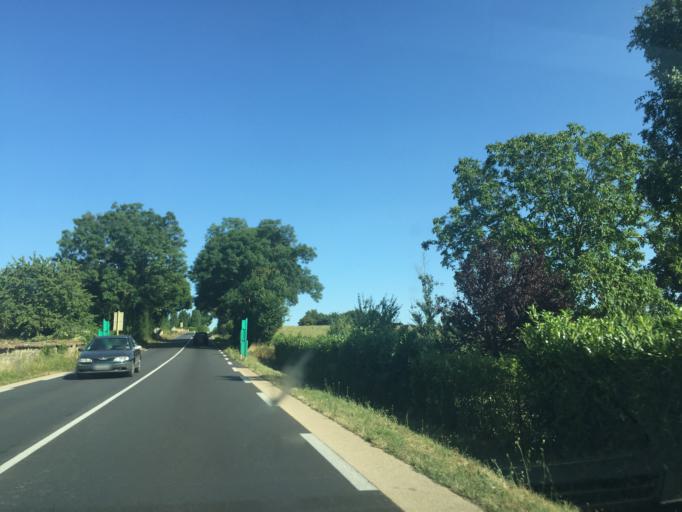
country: FR
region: Poitou-Charentes
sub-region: Departement des Deux-Sevres
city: Melle
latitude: 46.2173
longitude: -0.1245
